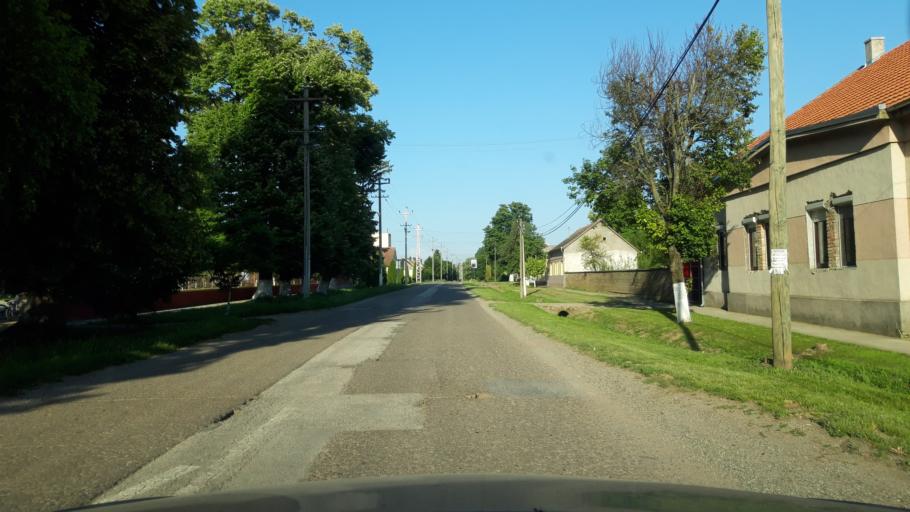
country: HR
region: Vukovarsko-Srijemska
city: Ilok
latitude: 45.1011
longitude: 19.4489
